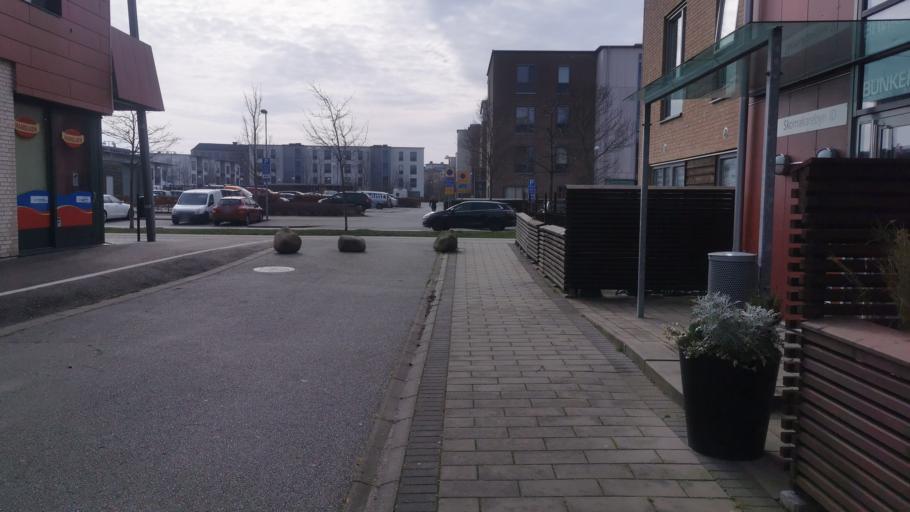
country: SE
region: Skane
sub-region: Malmo
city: Bunkeflostrand
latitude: 55.5584
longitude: 12.9323
